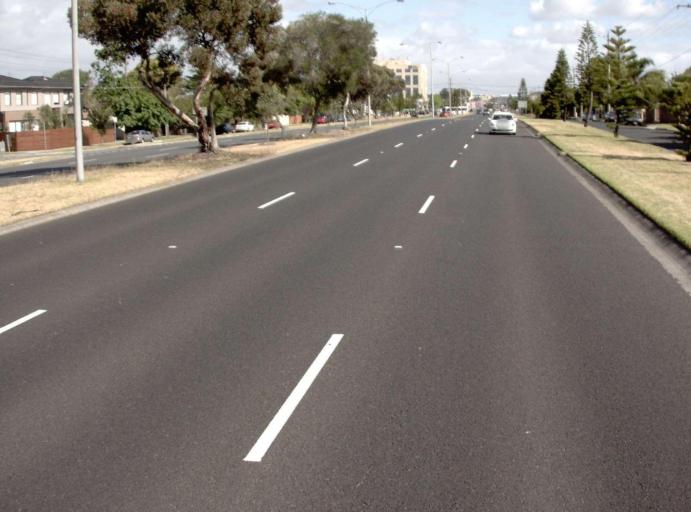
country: AU
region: Victoria
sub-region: Bayside
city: Cheltenham
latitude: -37.9699
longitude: 145.0613
